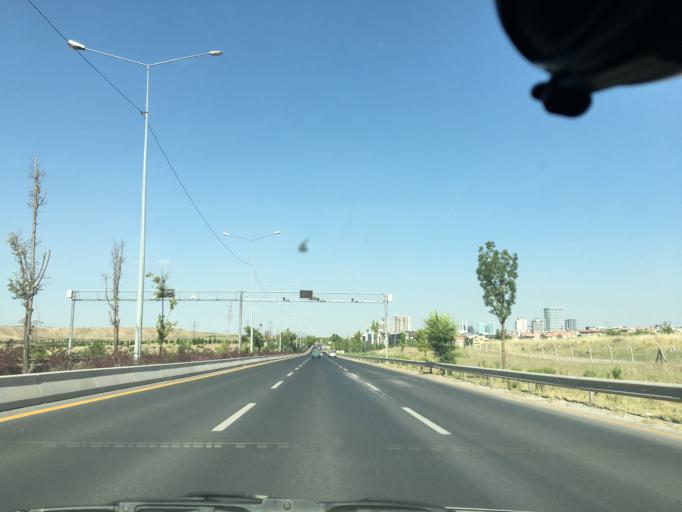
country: TR
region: Ankara
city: Batikent
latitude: 39.9157
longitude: 32.7597
